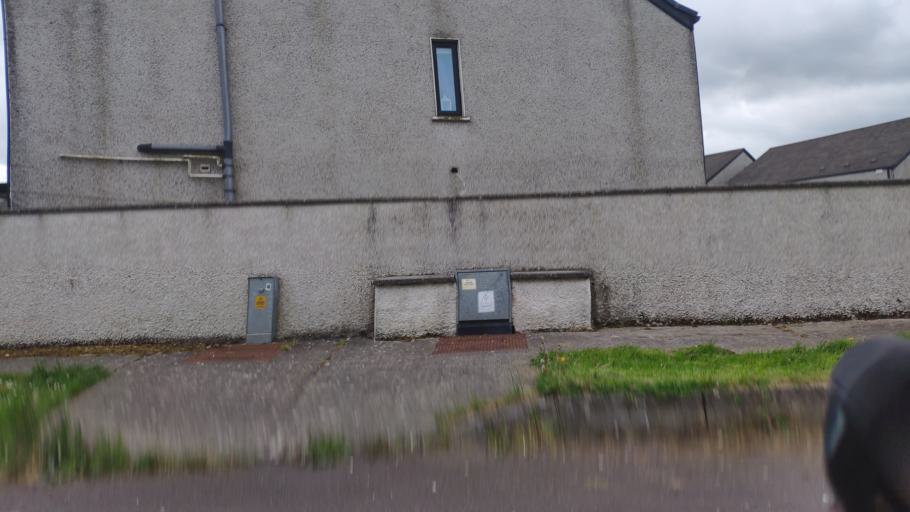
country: IE
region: Munster
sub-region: County Cork
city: Cork
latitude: 51.9117
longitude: -8.5042
